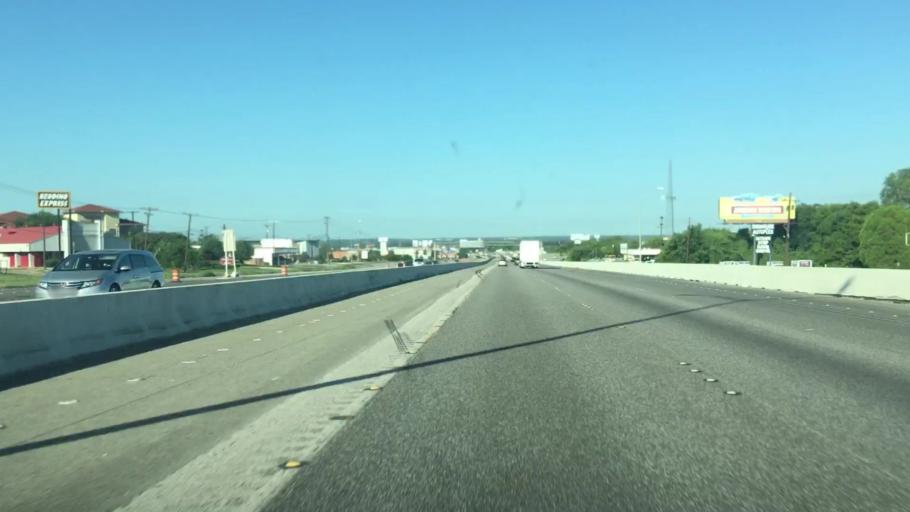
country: US
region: Texas
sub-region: Bell County
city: Temple
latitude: 31.0888
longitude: -97.3933
